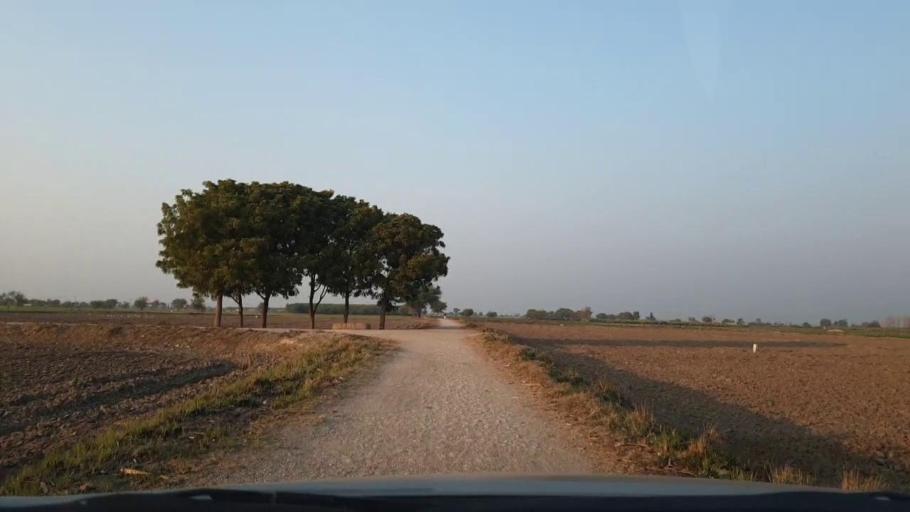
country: PK
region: Sindh
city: Tando Adam
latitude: 25.7139
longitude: 68.5793
